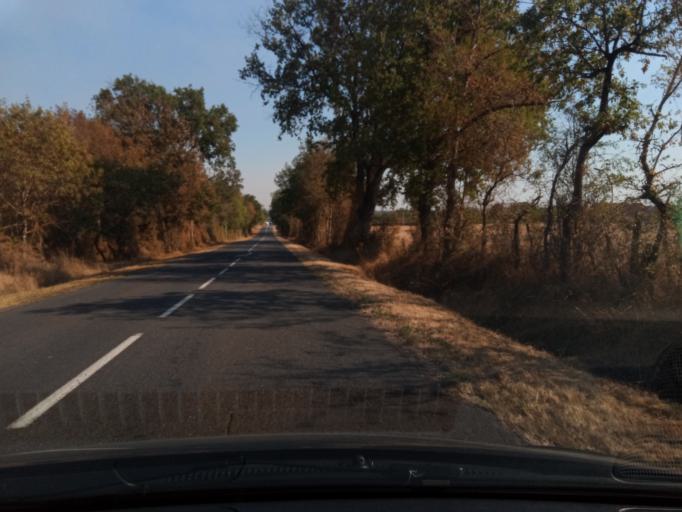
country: FR
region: Poitou-Charentes
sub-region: Departement de la Vienne
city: Montmorillon
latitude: 46.4336
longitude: 0.8444
